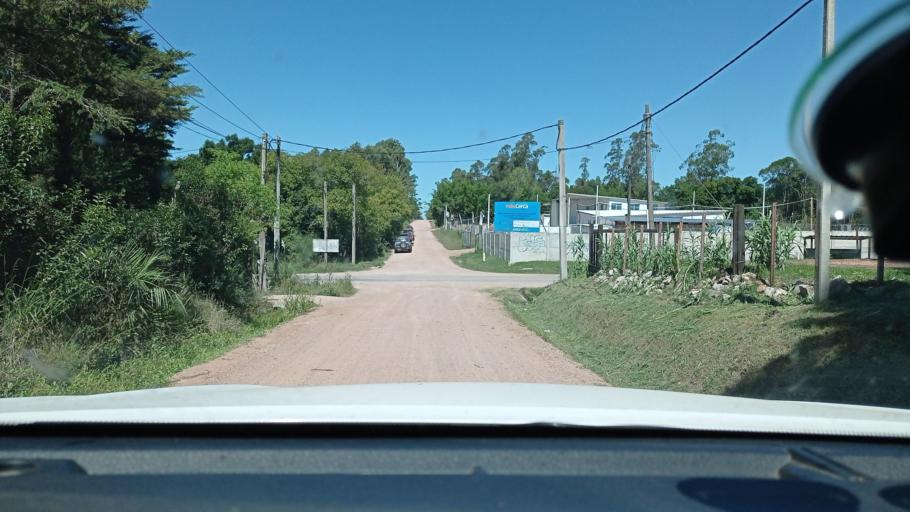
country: UY
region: Canelones
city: La Paz
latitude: -34.7534
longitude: -56.1913
